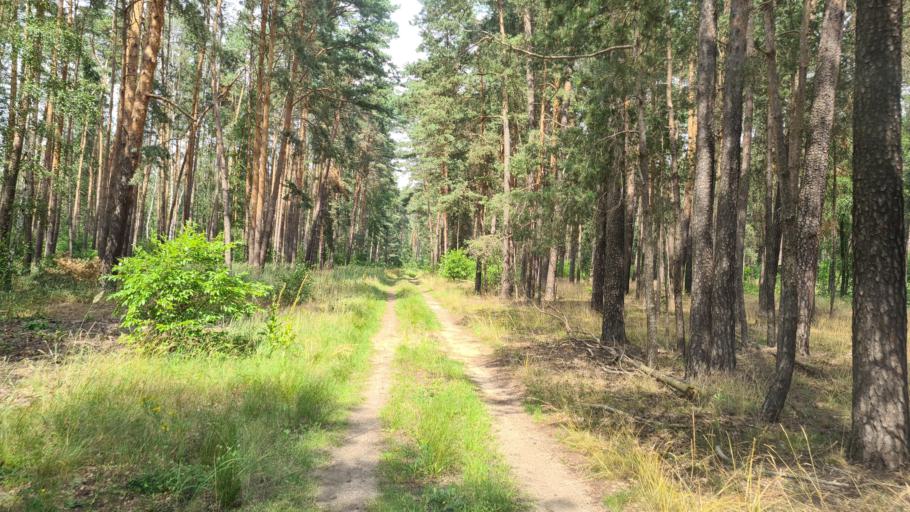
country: DE
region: Brandenburg
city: Bronkow
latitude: 51.7114
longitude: 13.8765
